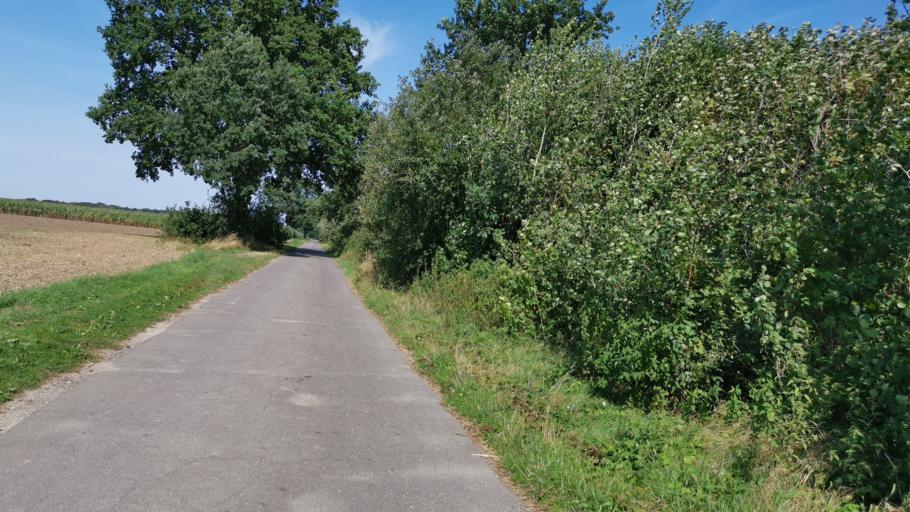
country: DE
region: Schleswig-Holstein
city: Gudow
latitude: 53.5654
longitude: 10.7702
